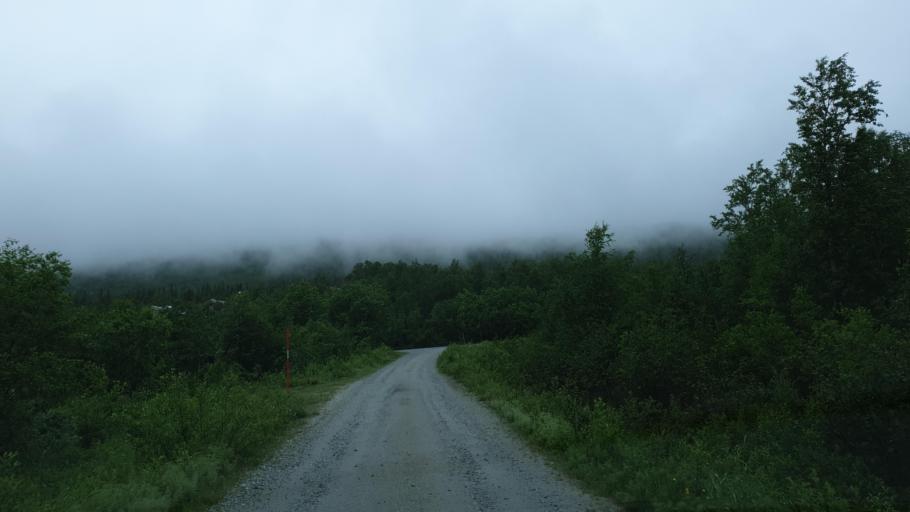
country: SE
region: Vaesterbotten
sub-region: Vilhelmina Kommun
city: Sjoberg
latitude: 65.2522
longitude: 15.5131
